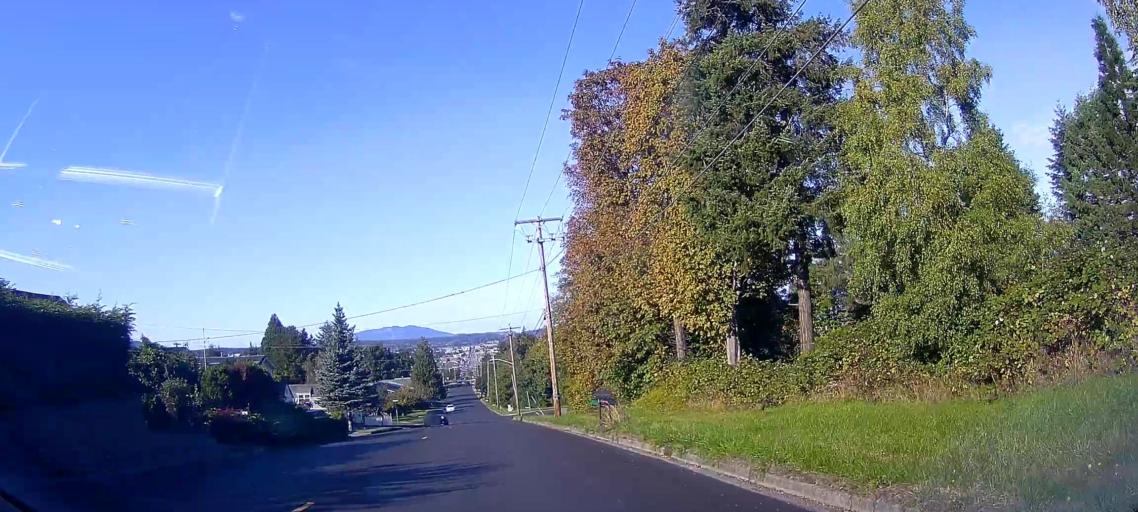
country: US
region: Washington
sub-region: Skagit County
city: Anacortes
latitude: 48.4894
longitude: -122.6129
